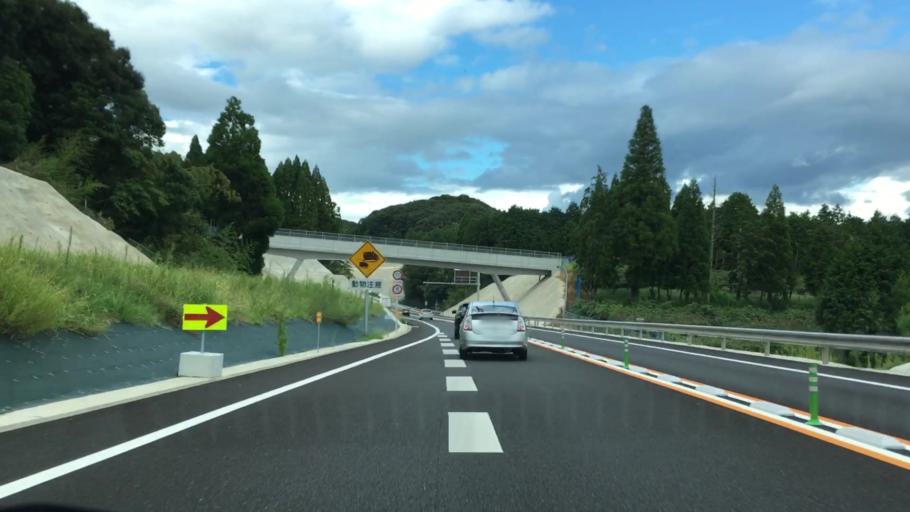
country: JP
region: Saga Prefecture
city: Imaricho-ko
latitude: 33.2997
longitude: 129.9145
